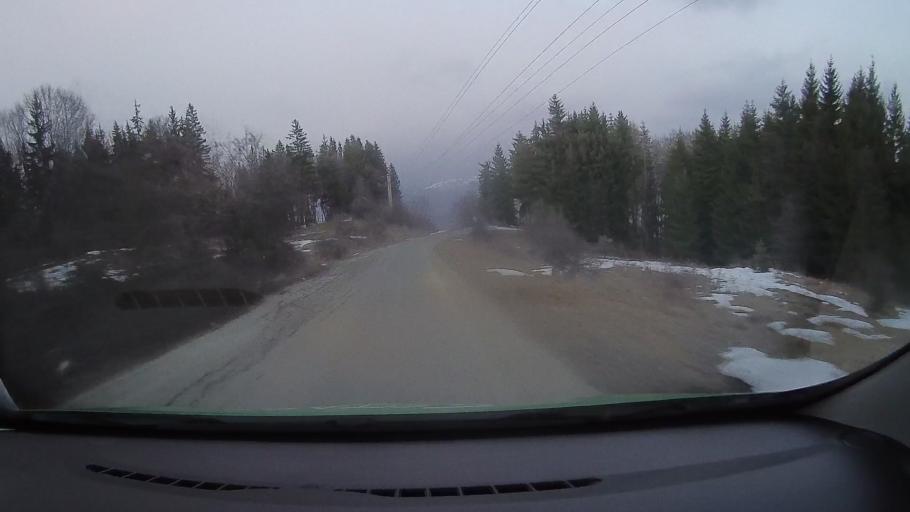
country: RO
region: Prahova
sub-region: Comuna Secaria
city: Secaria
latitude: 45.2903
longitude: 25.7038
